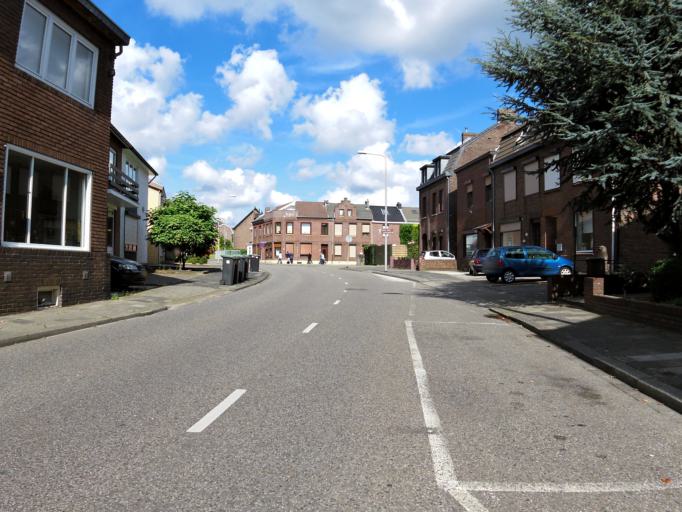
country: NL
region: Limburg
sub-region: Gemeente Kerkrade
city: Kerkrade
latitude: 50.8569
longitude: 6.0244
